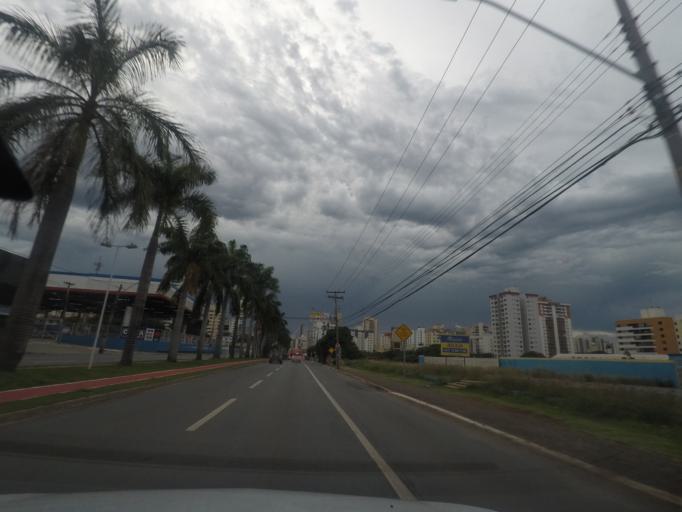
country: BR
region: Goias
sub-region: Goiania
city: Goiania
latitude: -16.7138
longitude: -49.2564
